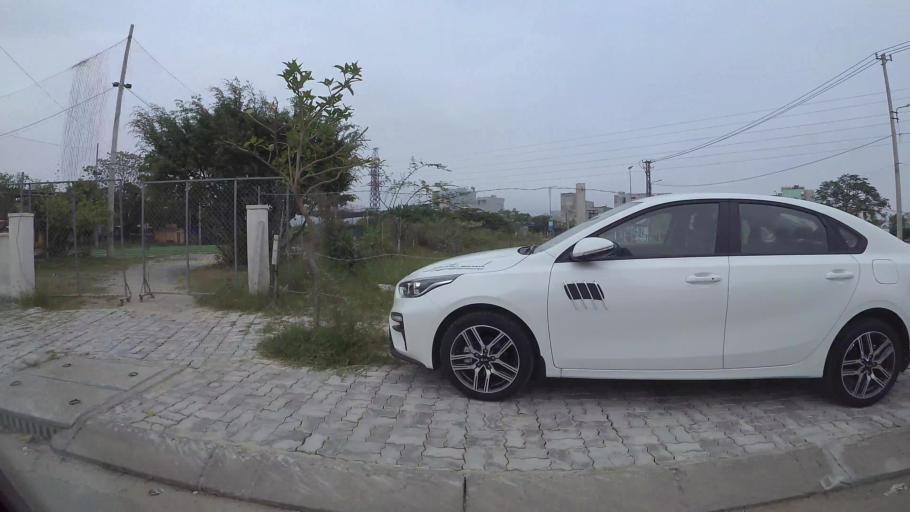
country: VN
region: Da Nang
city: Lien Chieu
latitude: 16.0667
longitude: 108.1702
